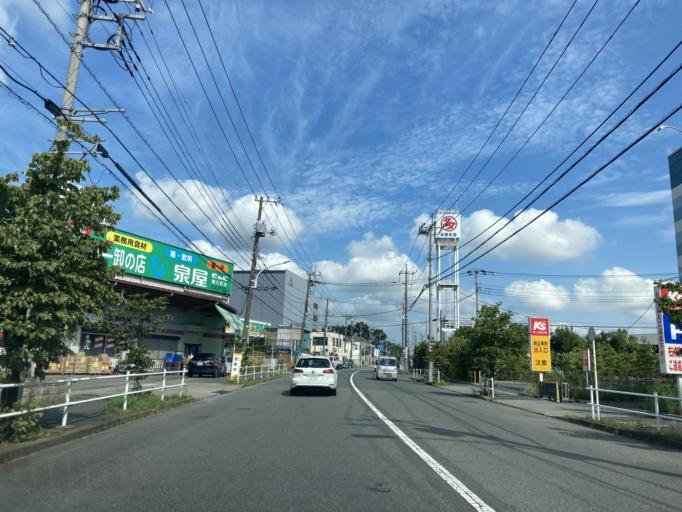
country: JP
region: Tokyo
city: Higashimurayama-shi
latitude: 35.7564
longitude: 139.4966
